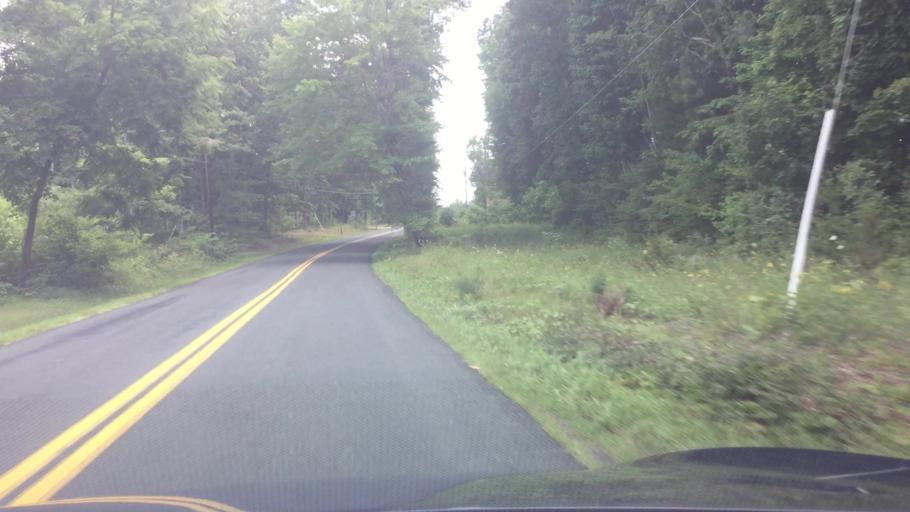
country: US
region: Virginia
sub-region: Appomattox County
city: Appomattox
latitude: 37.2876
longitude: -78.8519
